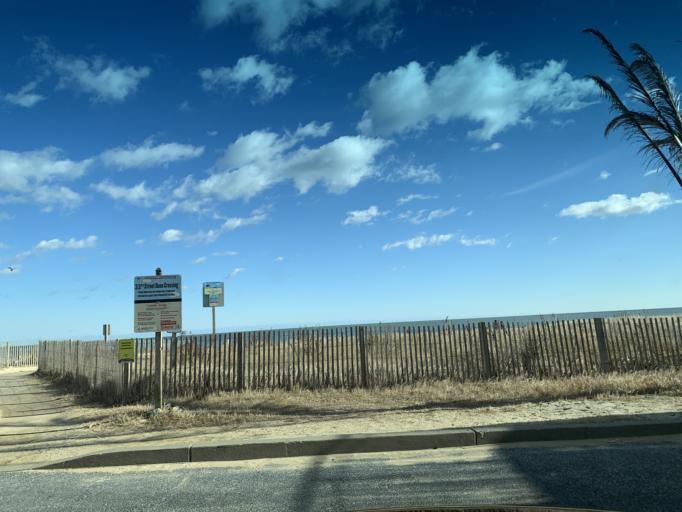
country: US
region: Maryland
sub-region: Worcester County
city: Ocean City
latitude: 38.3612
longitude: -75.0710
